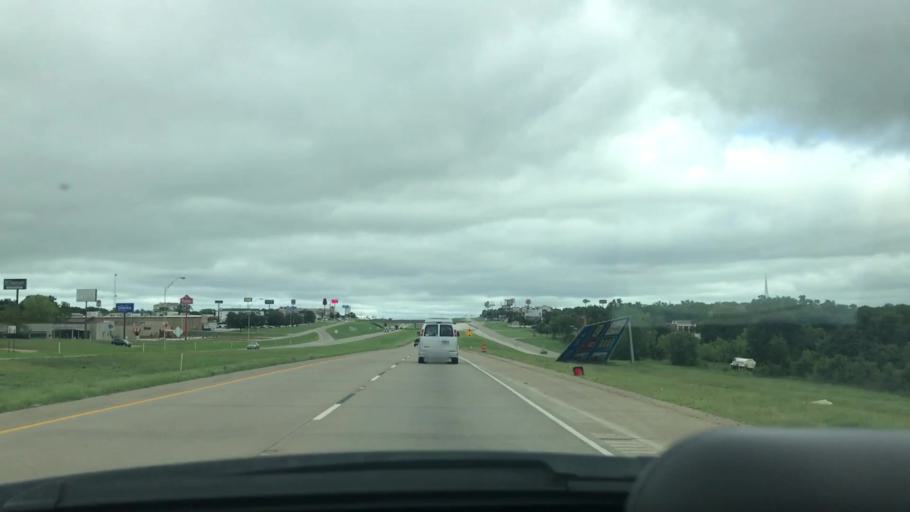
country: US
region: Texas
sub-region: Grayson County
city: Denison
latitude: 33.7546
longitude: -96.5852
